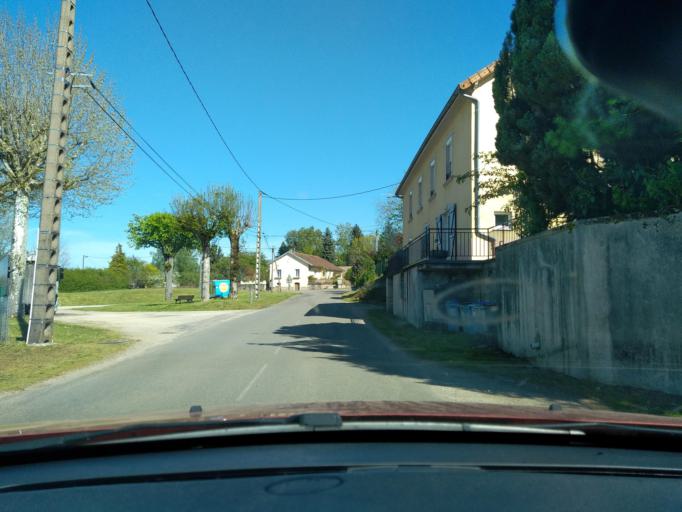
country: FR
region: Franche-Comte
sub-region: Departement du Jura
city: Cousance
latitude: 46.5793
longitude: 5.4308
